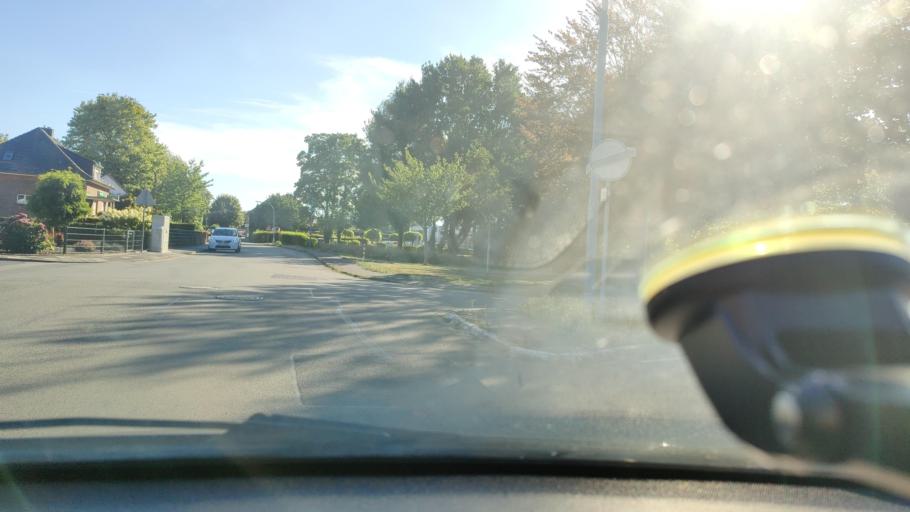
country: DE
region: North Rhine-Westphalia
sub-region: Regierungsbezirk Dusseldorf
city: Kleve
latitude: 51.7690
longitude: 6.2004
